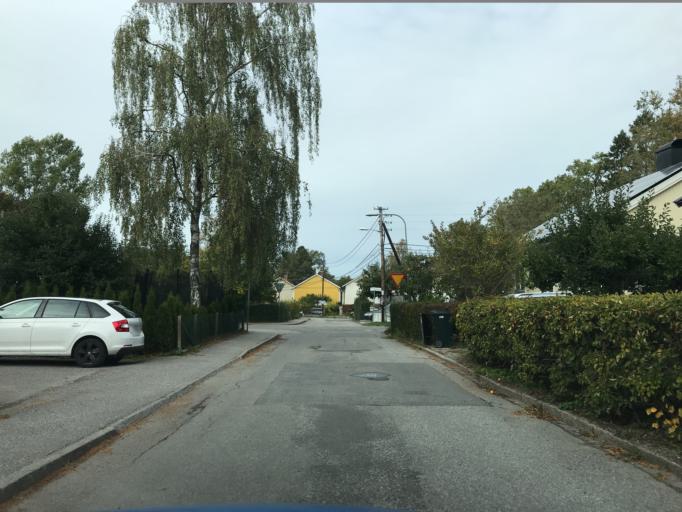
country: SE
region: Stockholm
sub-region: Huddinge Kommun
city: Segeltorp
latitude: 59.2750
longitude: 17.9689
